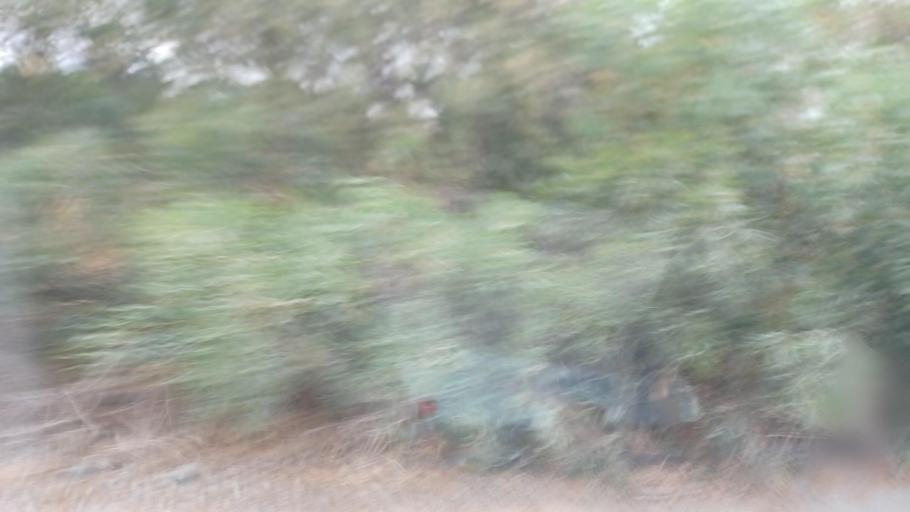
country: CY
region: Ammochostos
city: Ayia Napa
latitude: 35.0148
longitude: 34.0197
